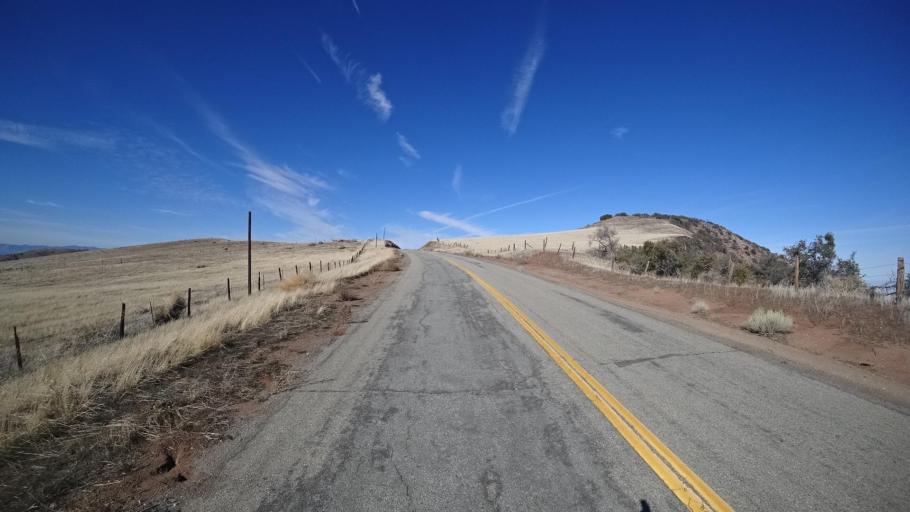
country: US
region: California
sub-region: Kern County
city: Maricopa
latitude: 34.8868
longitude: -119.3548
